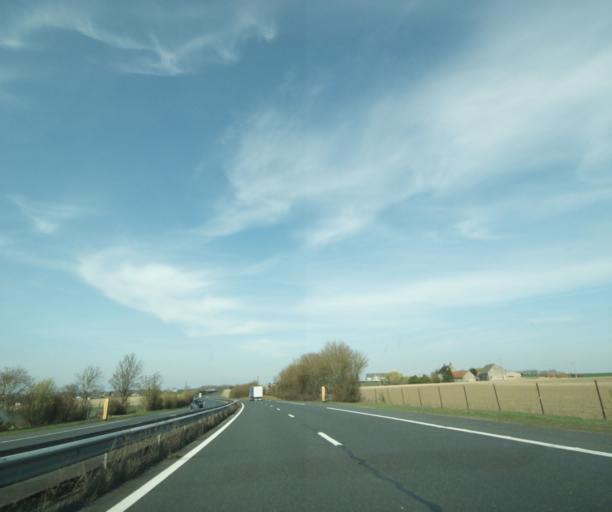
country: FR
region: Centre
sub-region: Departement de l'Indre
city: Vatan
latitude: 47.0610
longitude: 1.8199
